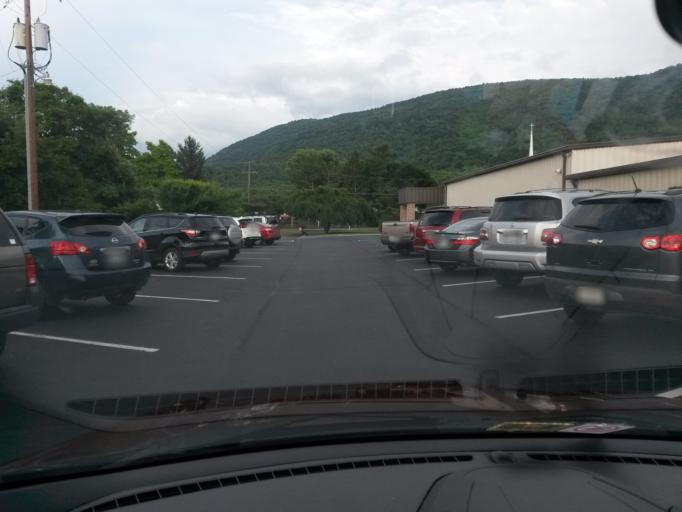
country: US
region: Virginia
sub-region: City of Covington
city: Fairlawn
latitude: 37.7652
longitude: -79.9686
